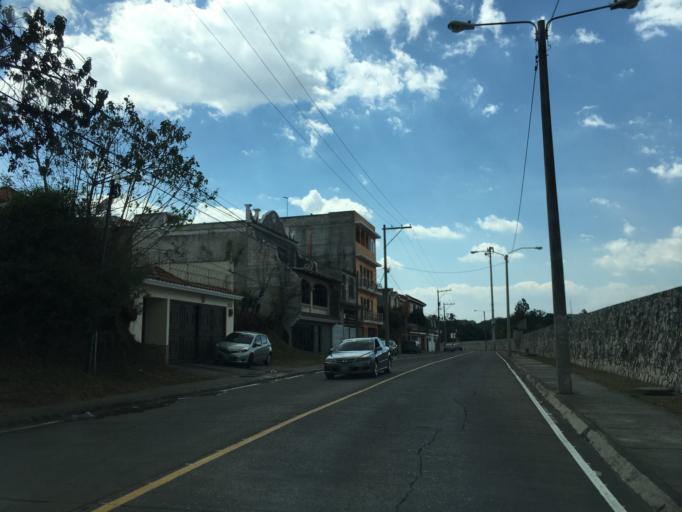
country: GT
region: Guatemala
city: Guatemala City
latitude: 14.6260
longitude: -90.4622
